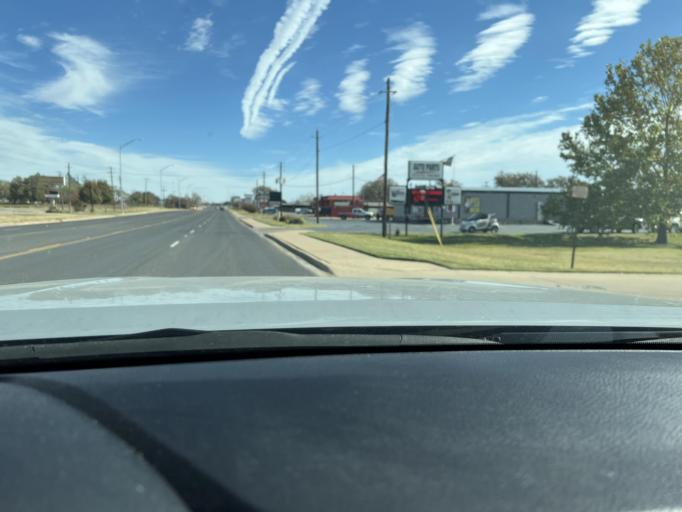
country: US
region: Texas
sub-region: Eastland County
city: Eastland
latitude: 32.4017
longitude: -98.8066
